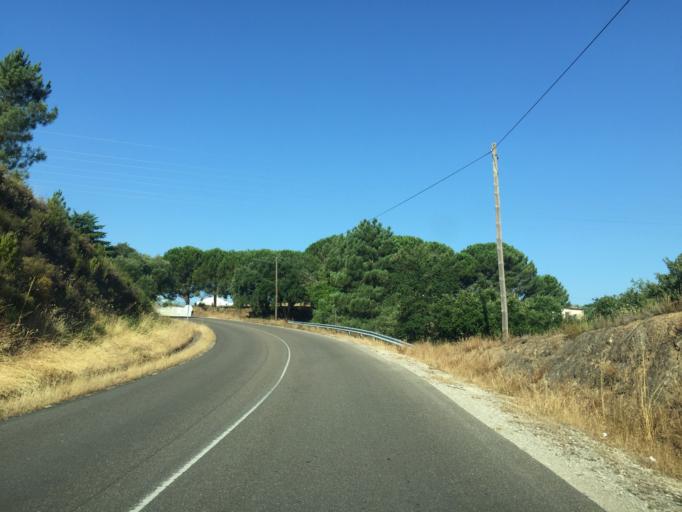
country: PT
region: Santarem
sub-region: Tomar
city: Tomar
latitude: 39.5920
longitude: -8.3472
